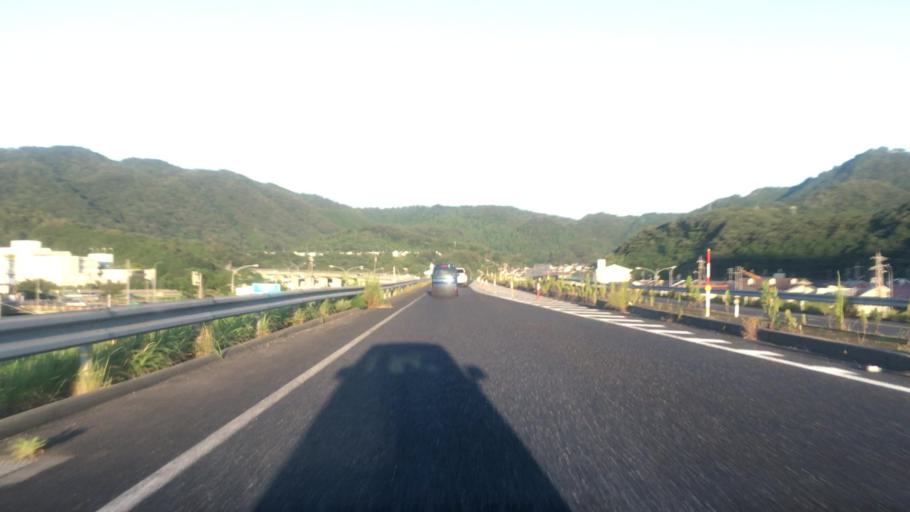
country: JP
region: Tottori
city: Tottori
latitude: 35.5235
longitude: 134.2272
